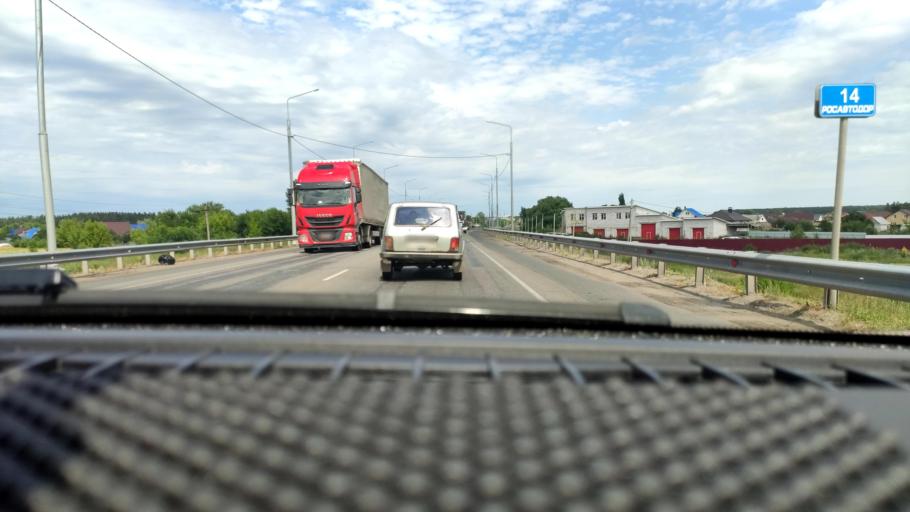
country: RU
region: Voronezj
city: Somovo
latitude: 51.6861
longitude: 39.3522
